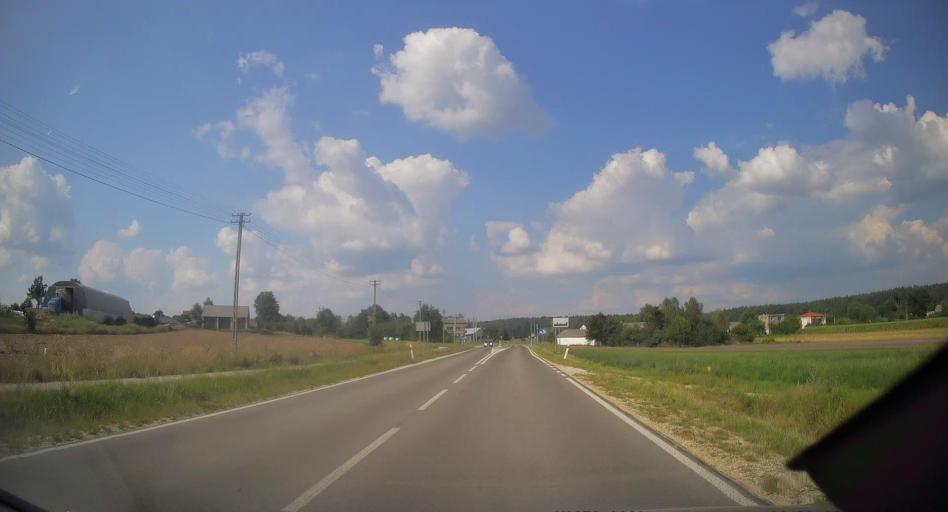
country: PL
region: Swietokrzyskie
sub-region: Powiat kielecki
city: Lopuszno
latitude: 50.9975
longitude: 20.2686
